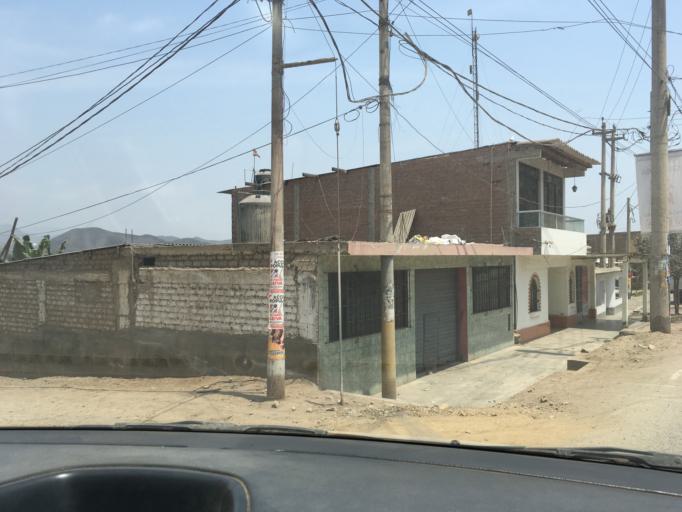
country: PE
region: Lima
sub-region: Lima
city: Cieneguilla
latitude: -12.1869
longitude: -76.8665
